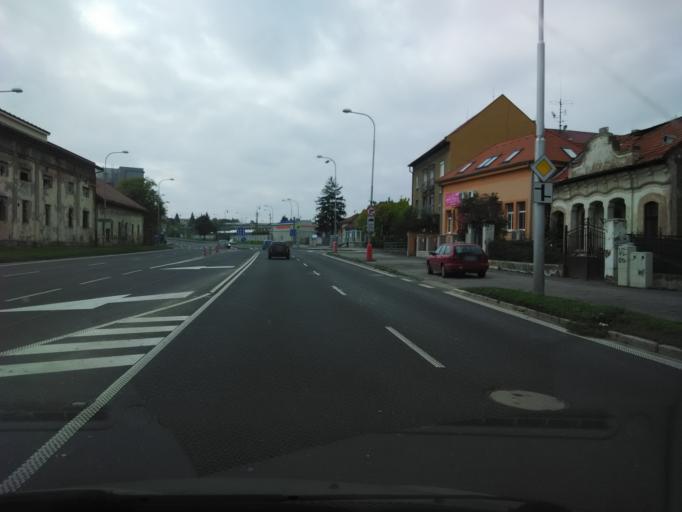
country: SK
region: Nitriansky
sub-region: Okres Nitra
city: Nitra
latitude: 48.3014
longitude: 18.0822
